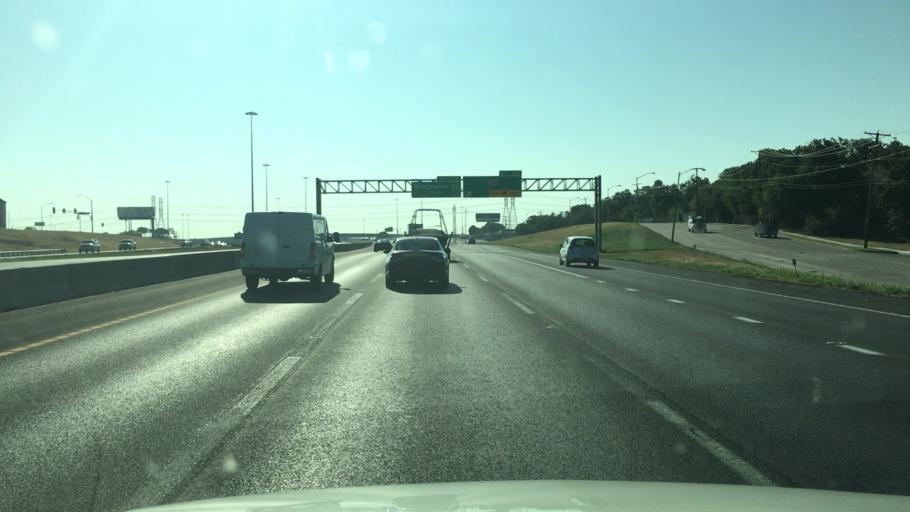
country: US
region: Texas
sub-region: Tarrant County
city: Richland Hills
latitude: 32.7599
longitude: -97.2266
